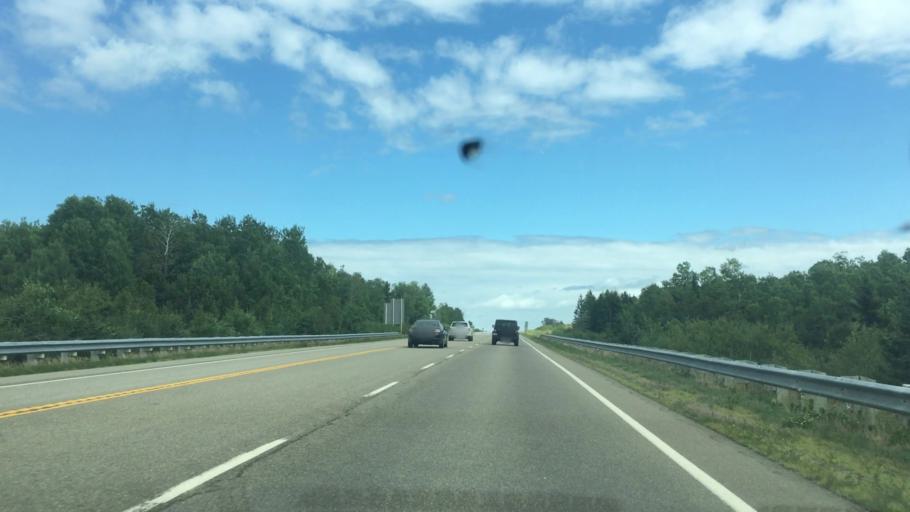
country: CA
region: Nova Scotia
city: Port Hawkesbury
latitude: 45.6223
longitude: -61.6077
